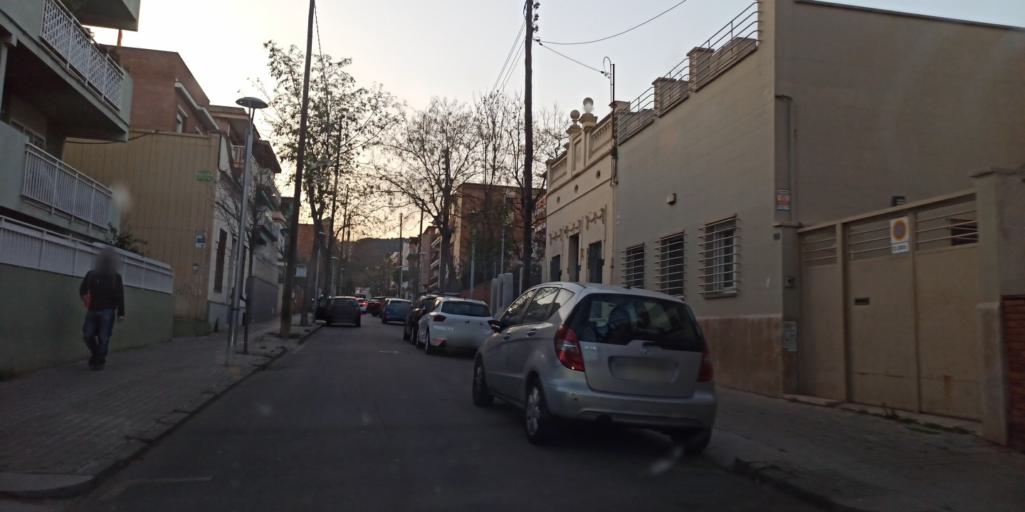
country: ES
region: Catalonia
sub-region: Provincia de Barcelona
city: Nou Barris
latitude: 41.4358
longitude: 2.1598
